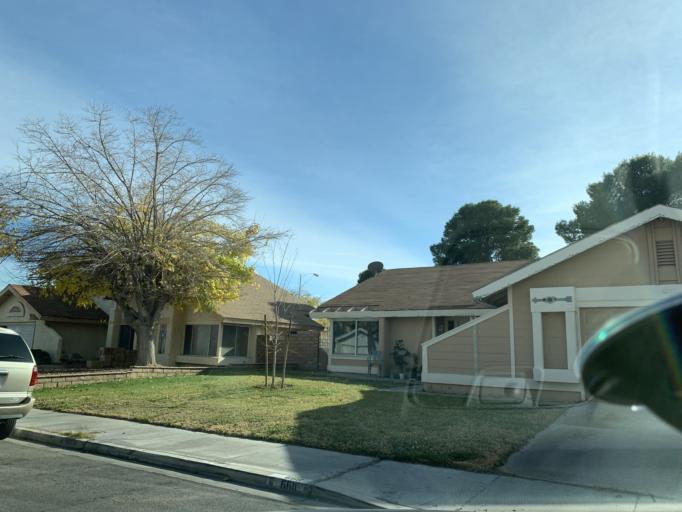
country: US
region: Nevada
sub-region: Clark County
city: Spring Valley
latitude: 36.1076
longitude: -115.2366
